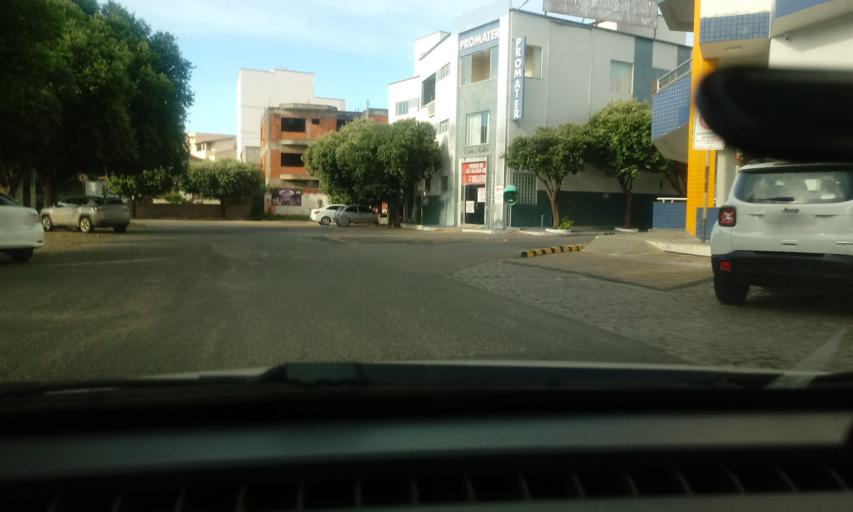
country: BR
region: Bahia
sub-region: Guanambi
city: Guanambi
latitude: -14.2263
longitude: -42.7807
